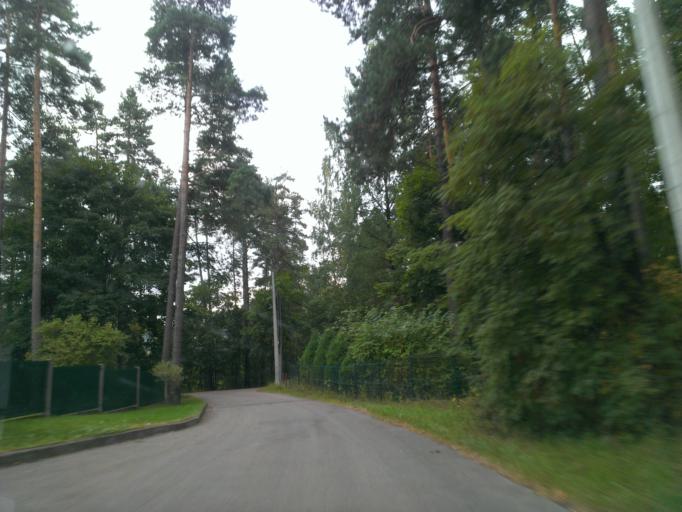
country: LV
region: Riga
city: Bergi
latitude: 56.9856
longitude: 24.3054
